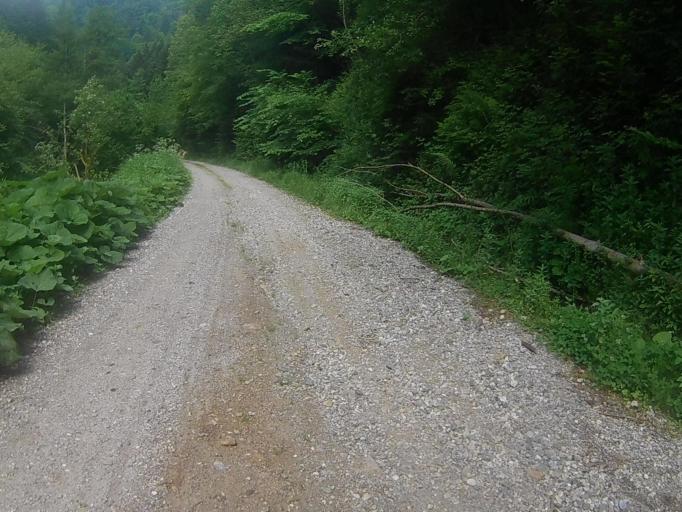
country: SI
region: Maribor
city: Bresternica
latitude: 46.6053
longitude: 15.5727
